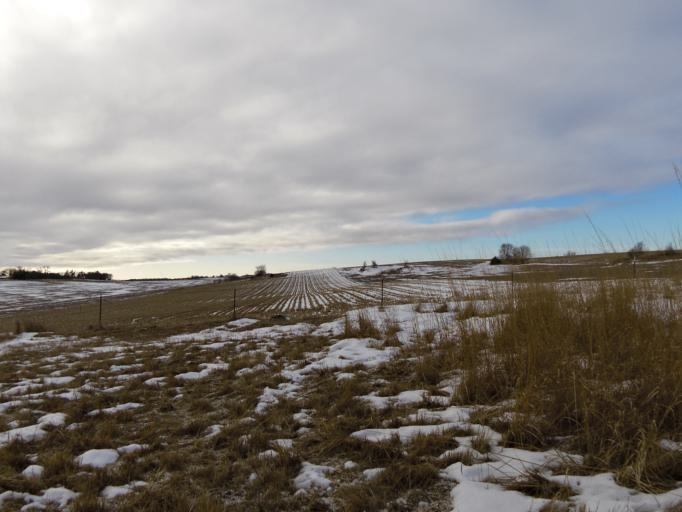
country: US
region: Wisconsin
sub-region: Pierce County
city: Prescott
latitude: 44.8022
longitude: -92.8317
